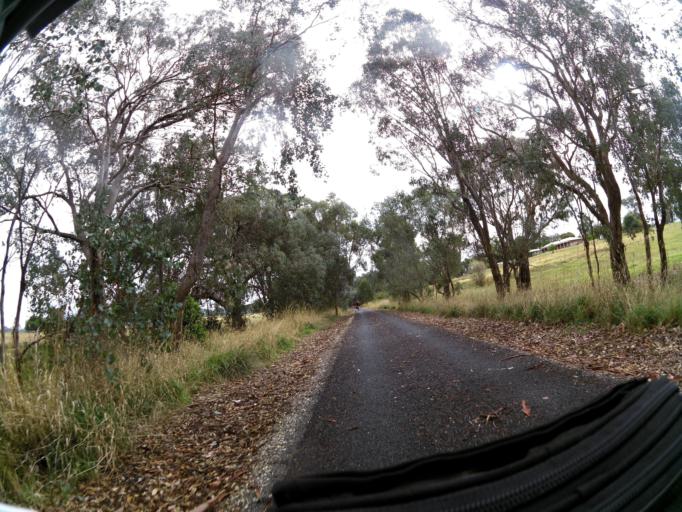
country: AU
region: New South Wales
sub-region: Albury Municipality
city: East Albury
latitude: -36.1434
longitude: 147.0027
